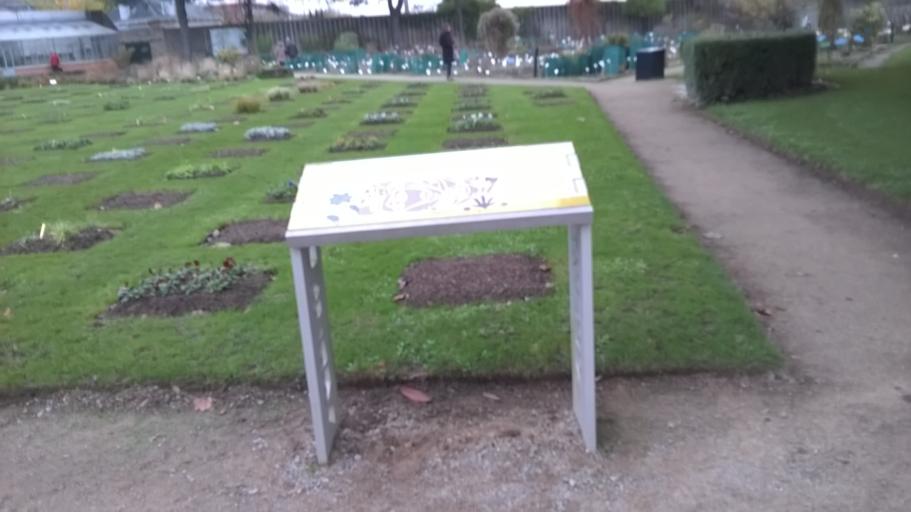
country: FR
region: Pays de la Loire
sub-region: Departement de la Loire-Atlantique
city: Nantes
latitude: 47.2210
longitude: -1.5438
